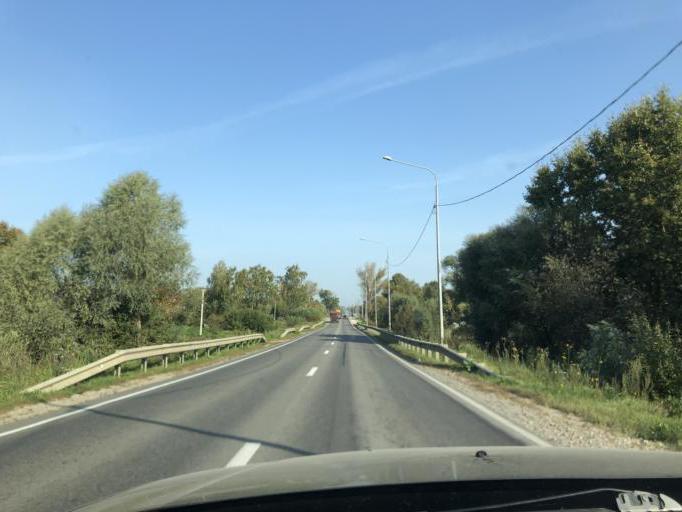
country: RU
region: Tula
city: Novogurovskiy
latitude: 54.4625
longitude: 37.4741
